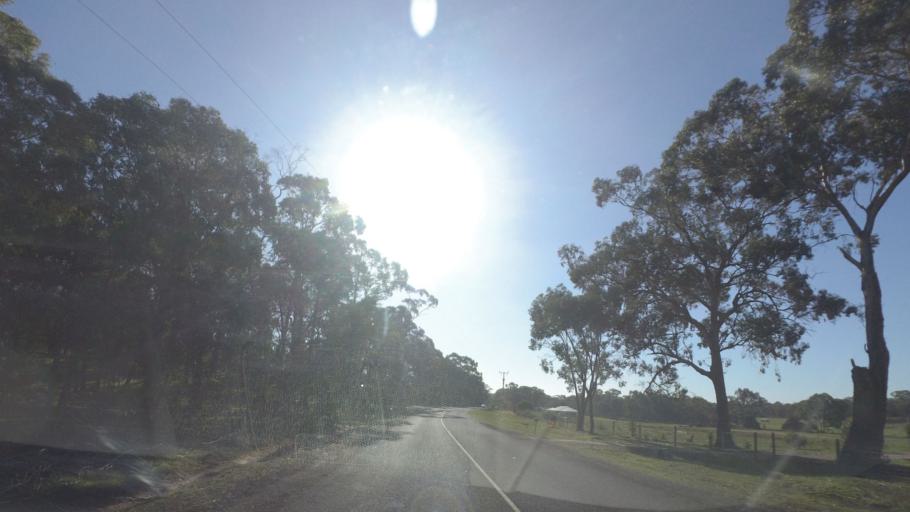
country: AU
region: Victoria
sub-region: Greater Bendigo
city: Kangaroo Flat
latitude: -36.8536
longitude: 144.2803
